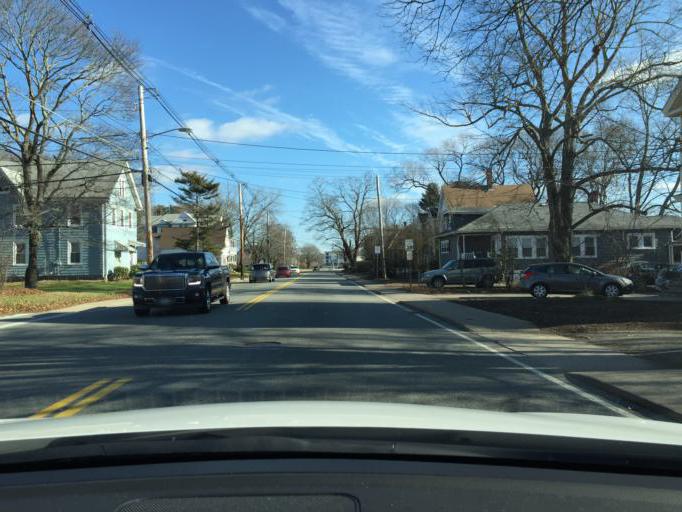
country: US
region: Massachusetts
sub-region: Bristol County
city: Mansfield
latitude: 42.0308
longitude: -71.2266
